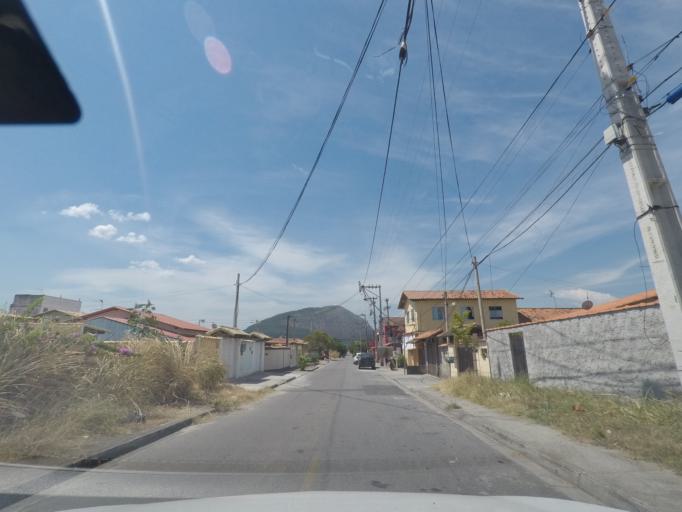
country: BR
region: Rio de Janeiro
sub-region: Marica
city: Marica
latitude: -22.9655
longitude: -42.9603
